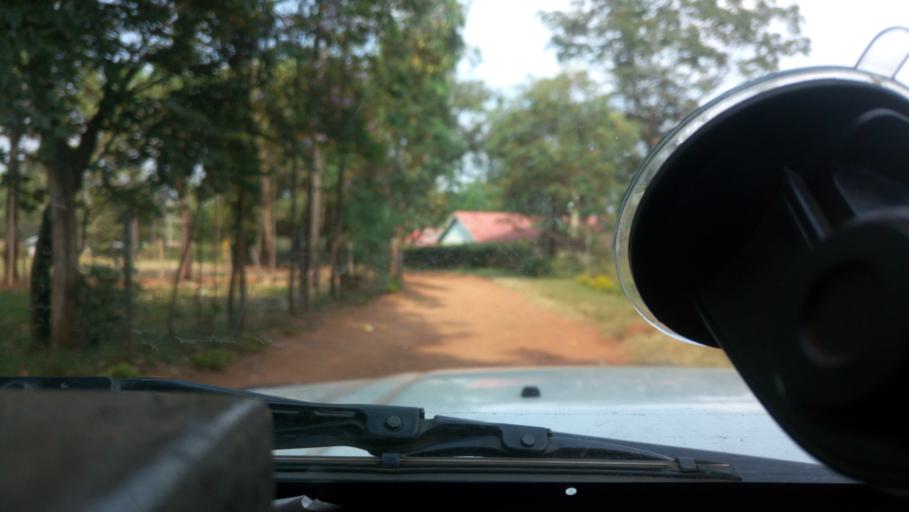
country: KE
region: Kisii
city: Ogembo
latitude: -0.7950
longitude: 34.5840
